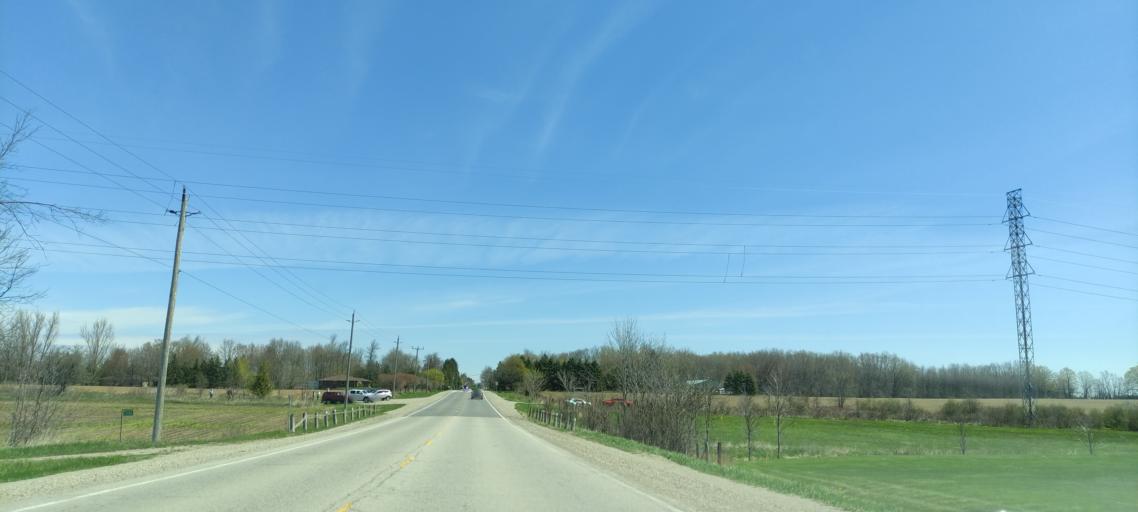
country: CA
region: Ontario
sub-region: Wellington County
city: Guelph
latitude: 43.5935
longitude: -80.3448
